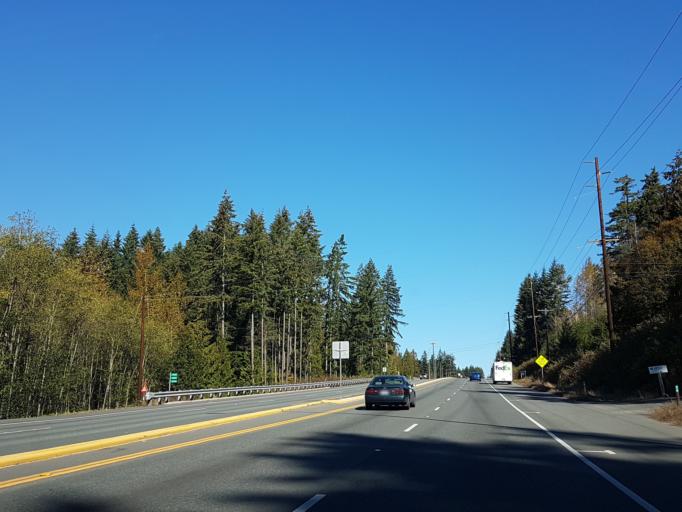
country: US
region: Washington
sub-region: Snohomish County
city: Clearview
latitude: 47.8157
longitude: -122.1395
